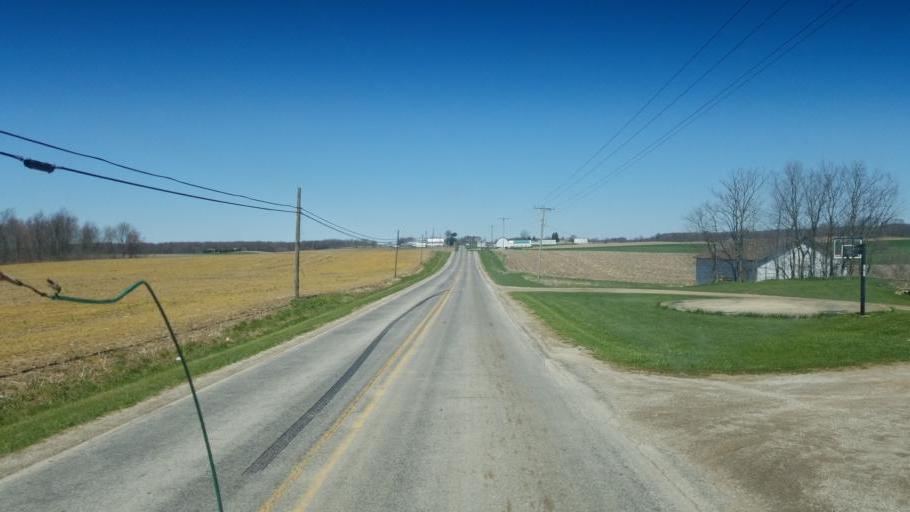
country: US
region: Ohio
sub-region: Richland County
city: Shelby
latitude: 40.9274
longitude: -82.5806
